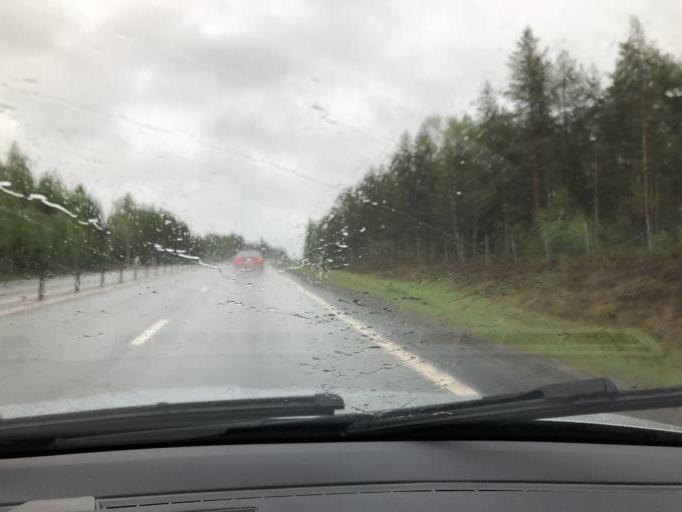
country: SE
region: Vaesterbotten
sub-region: Umea Kommun
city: Roback
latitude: 63.7381
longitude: 20.1128
